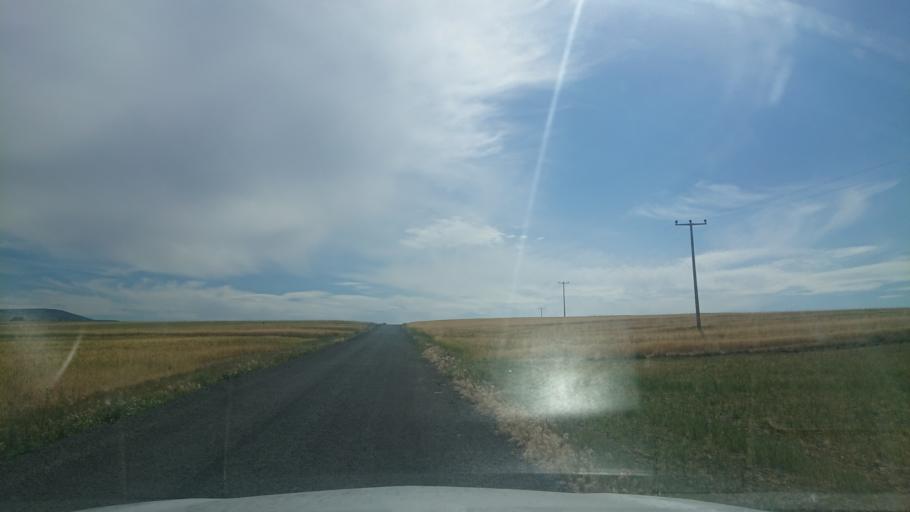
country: TR
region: Aksaray
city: Ortakoy
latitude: 38.8216
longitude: 34.0137
